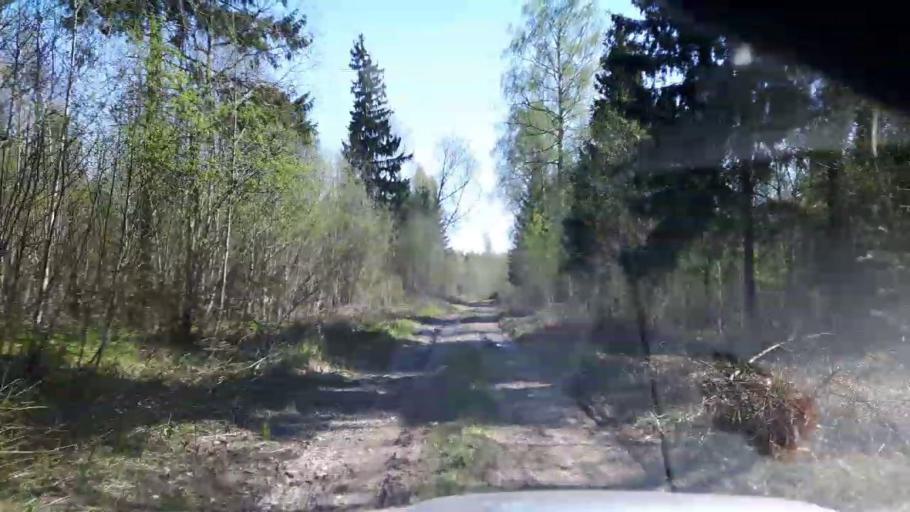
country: EE
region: Paernumaa
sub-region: Tootsi vald
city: Tootsi
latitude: 58.5442
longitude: 24.8020
